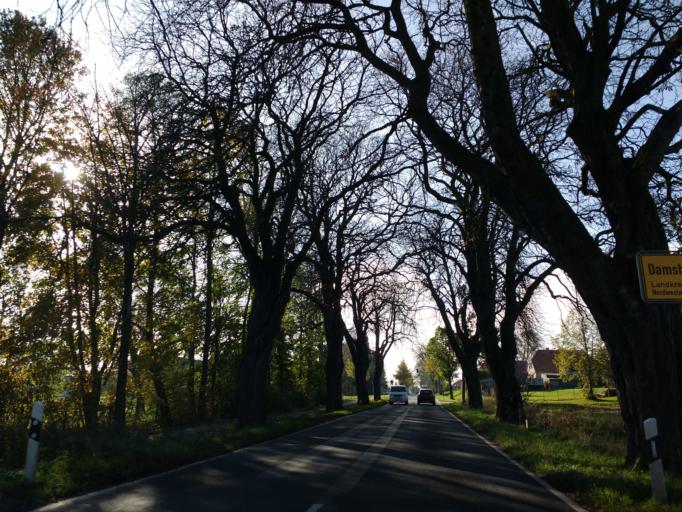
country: DE
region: Mecklenburg-Vorpommern
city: Klutz
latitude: 53.9331
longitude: 11.1530
